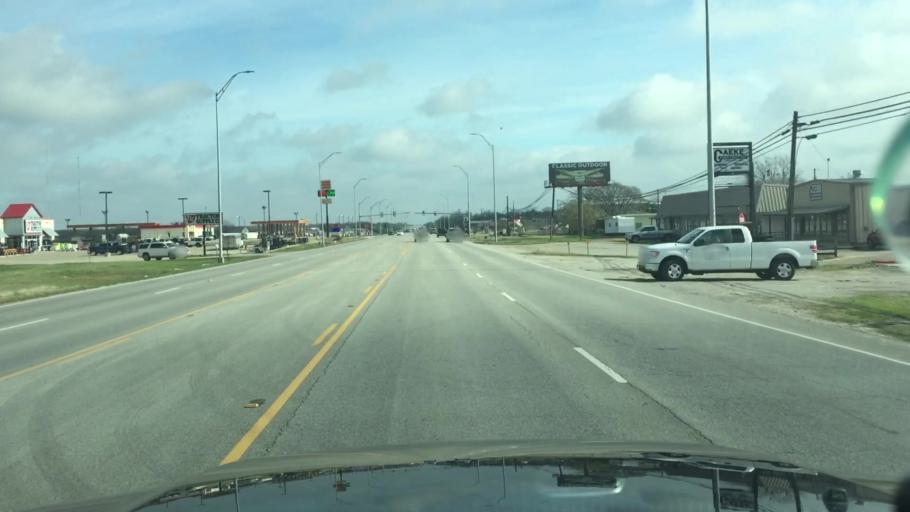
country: US
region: Texas
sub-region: Lee County
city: Giddings
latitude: 30.1787
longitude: -96.9101
